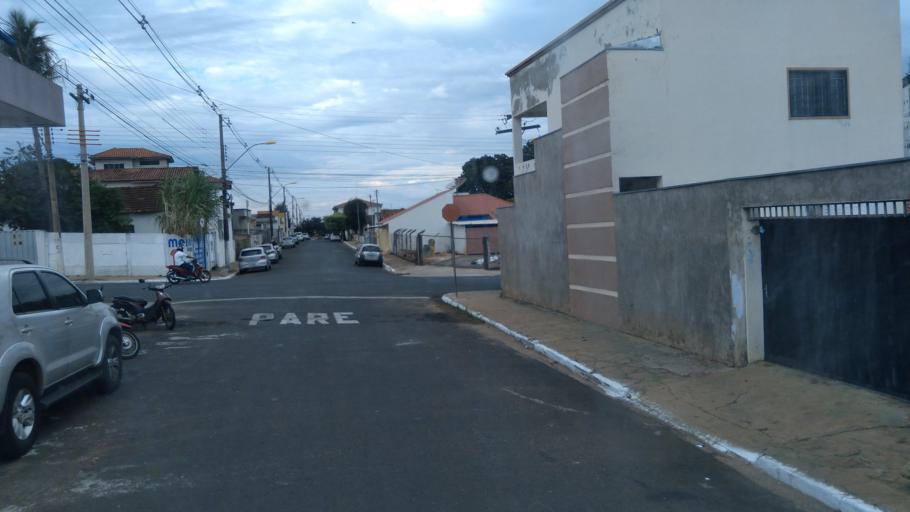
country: BR
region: Goias
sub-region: Mineiros
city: Mineiros
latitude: -17.5680
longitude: -52.5572
